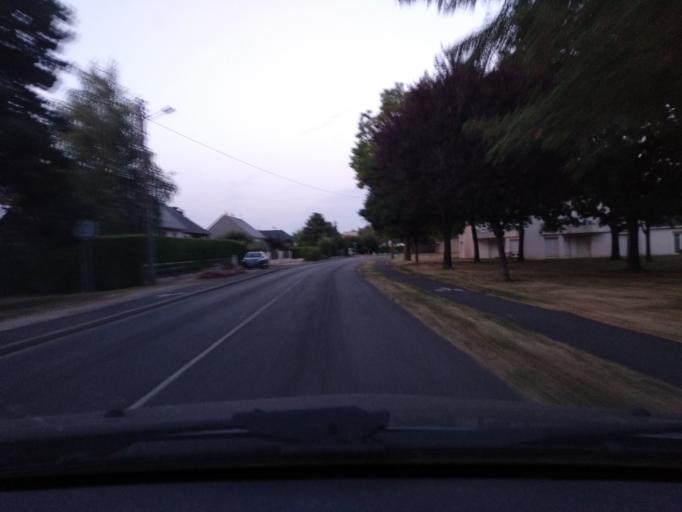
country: FR
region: Centre
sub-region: Departement d'Indre-et-Loire
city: Chanceaux-sur-Choisille
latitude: 47.4516
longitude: 0.7040
